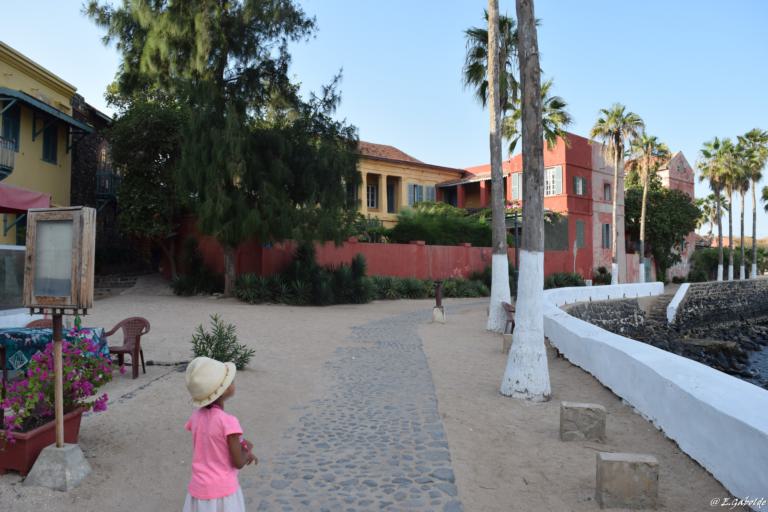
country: SN
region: Dakar
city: Dakar
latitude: 14.6695
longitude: -17.3997
